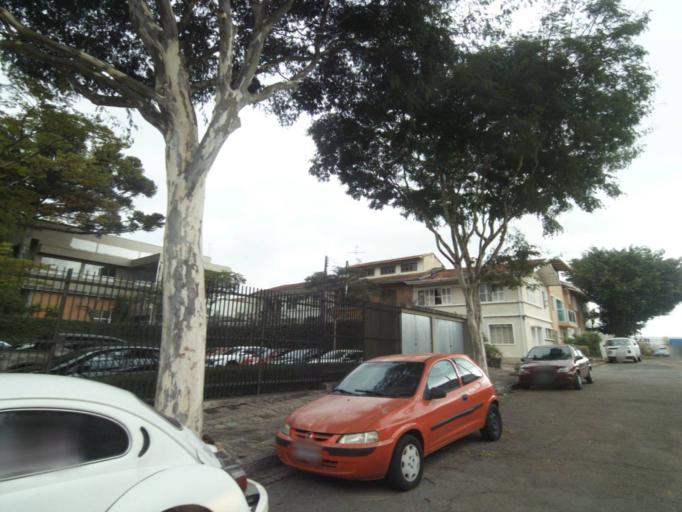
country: BR
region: Parana
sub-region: Curitiba
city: Curitiba
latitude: -25.4561
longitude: -49.2581
